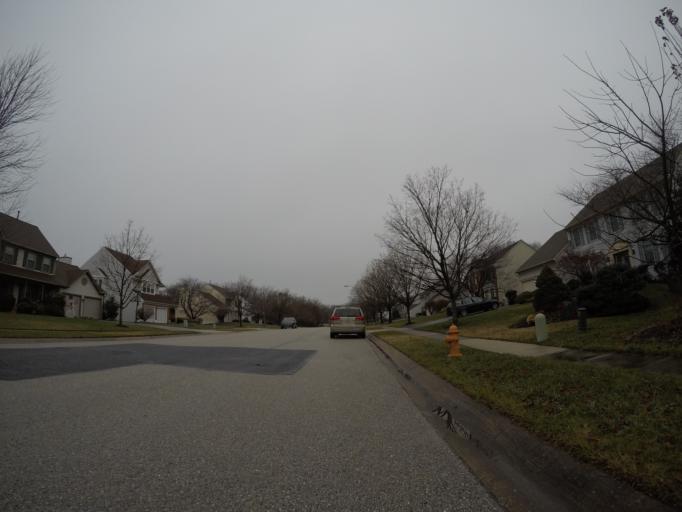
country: US
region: Maryland
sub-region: Howard County
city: Ilchester
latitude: 39.2273
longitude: -76.7946
